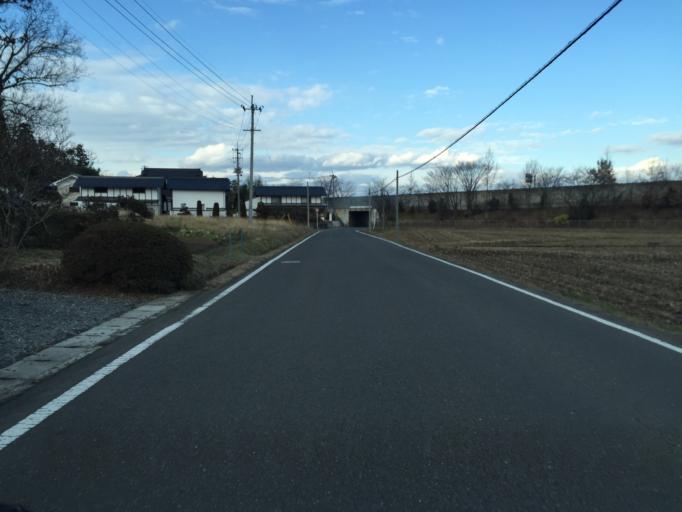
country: JP
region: Fukushima
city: Fukushima-shi
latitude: 37.7094
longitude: 140.4478
